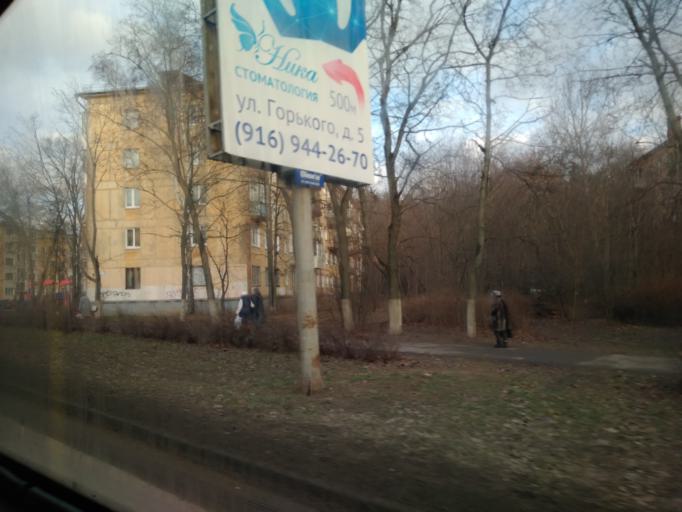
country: RU
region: Moskovskaya
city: Zhukovskiy
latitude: 55.5933
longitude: 38.1283
